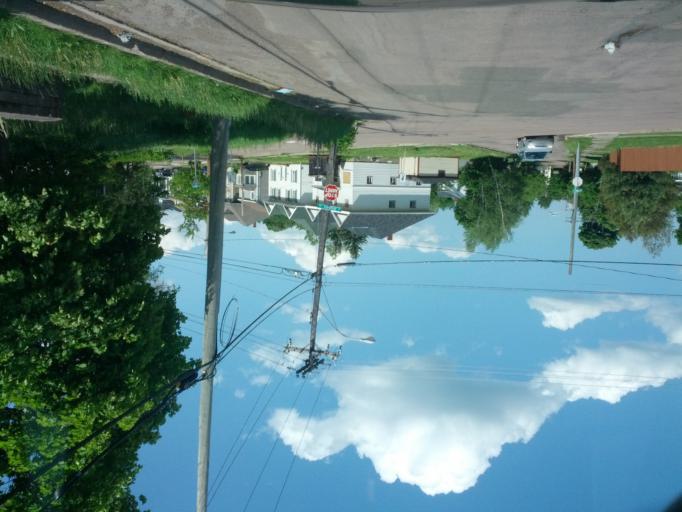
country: CA
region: New Brunswick
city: Moncton
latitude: 46.0956
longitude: -64.7763
